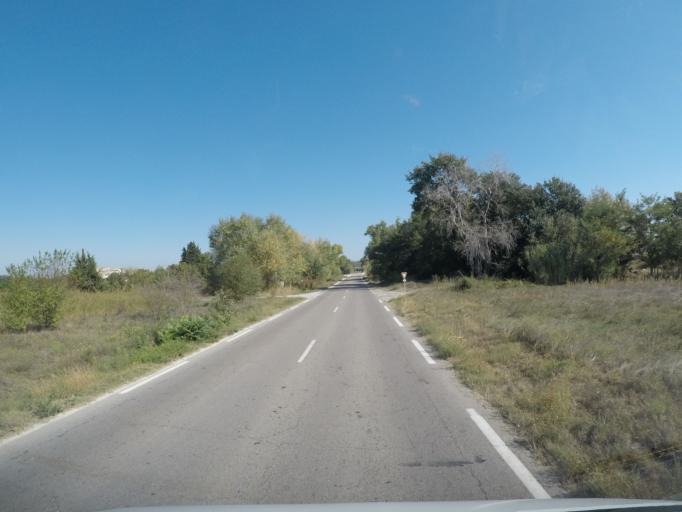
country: FR
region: Languedoc-Roussillon
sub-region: Departement du Gard
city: Moussac
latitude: 43.9731
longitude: 4.2249
